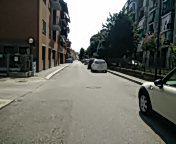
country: IT
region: Piedmont
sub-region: Provincia di Torino
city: Nichelino
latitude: 45.0241
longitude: 7.6524
